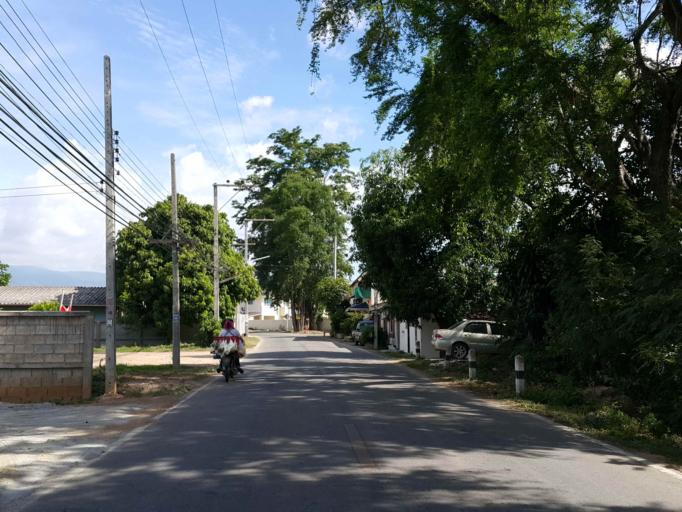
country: TH
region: Chiang Mai
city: Saraphi
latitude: 18.7313
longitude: 98.9978
